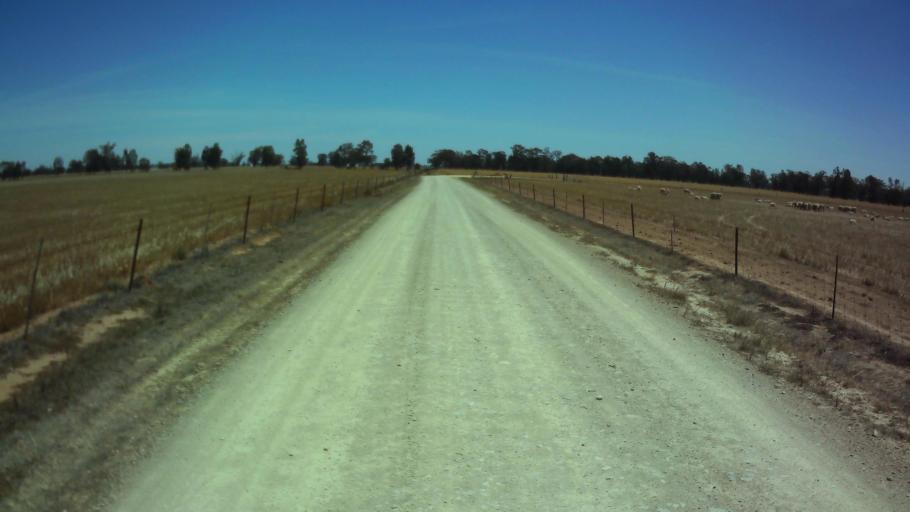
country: AU
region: New South Wales
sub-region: Weddin
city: Grenfell
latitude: -34.0544
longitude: 147.7681
